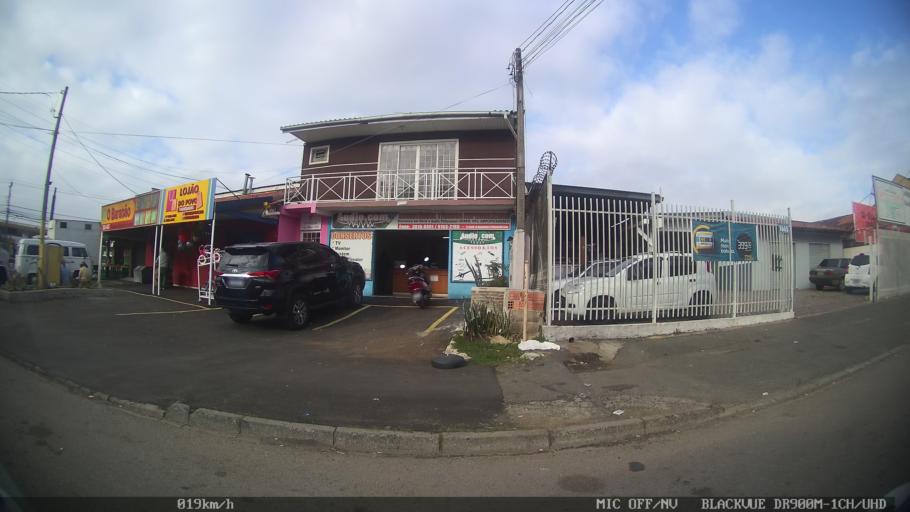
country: BR
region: Parana
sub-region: Curitiba
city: Curitiba
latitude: -25.3924
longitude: -49.3355
